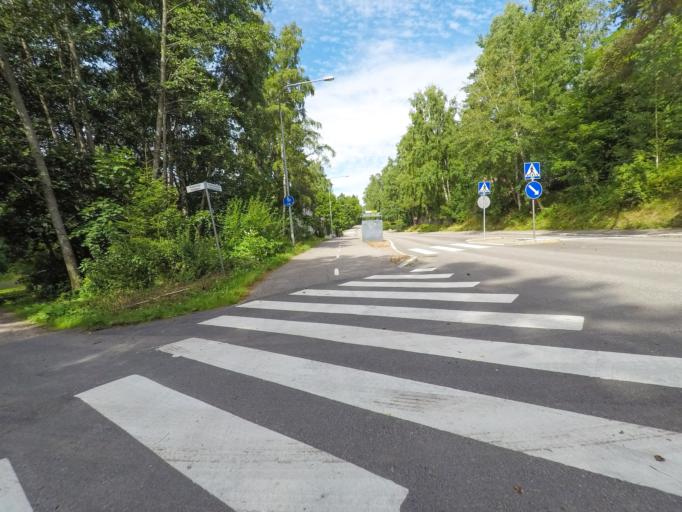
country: FI
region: Uusimaa
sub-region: Helsinki
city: Vantaa
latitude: 60.1674
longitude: 25.0807
